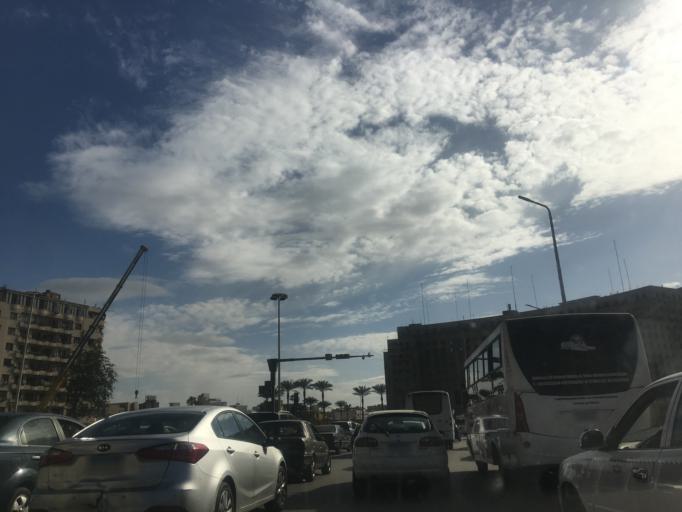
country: EG
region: Muhafazat al Qahirah
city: Cairo
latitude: 30.0452
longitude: 31.2352
